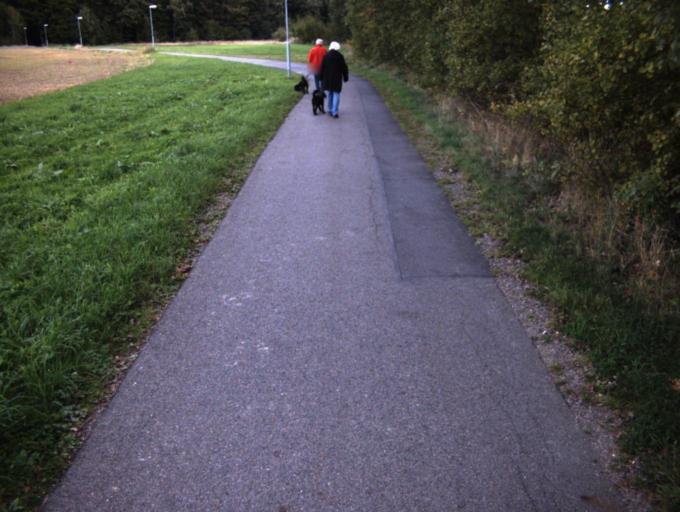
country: SE
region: Skane
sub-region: Helsingborg
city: Helsingborg
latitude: 56.0843
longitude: 12.6762
